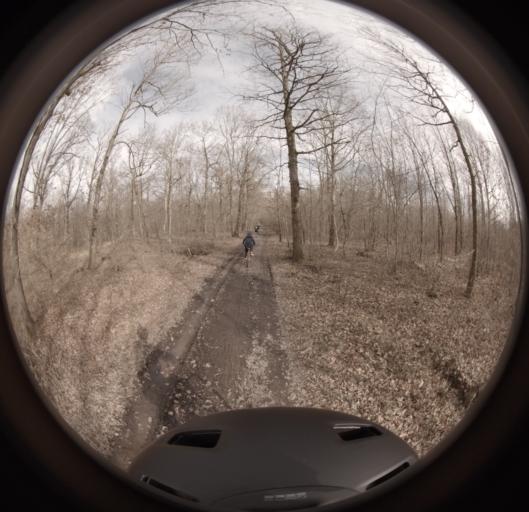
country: FR
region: Midi-Pyrenees
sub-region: Departement du Tarn-et-Garonne
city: Montech
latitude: 43.9590
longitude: 1.2775
